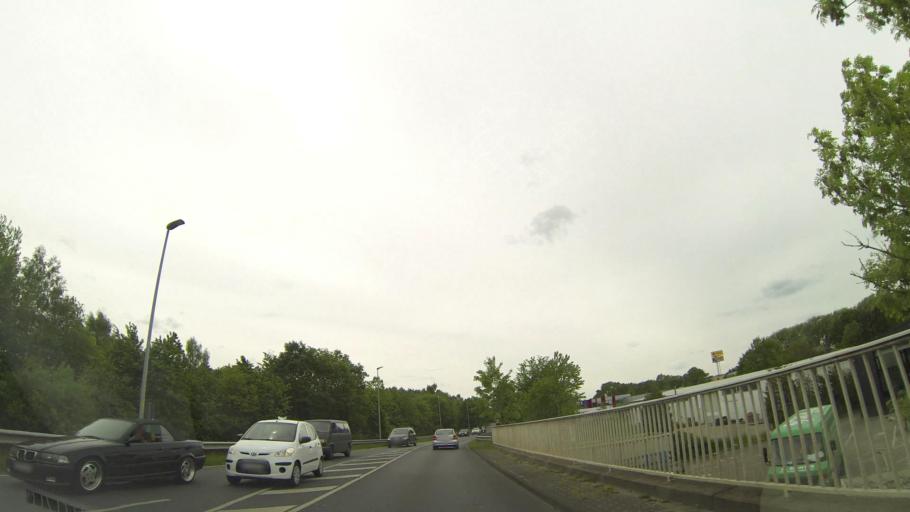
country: DE
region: Schleswig-Holstein
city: Halstenbek
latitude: 53.6272
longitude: 9.8689
